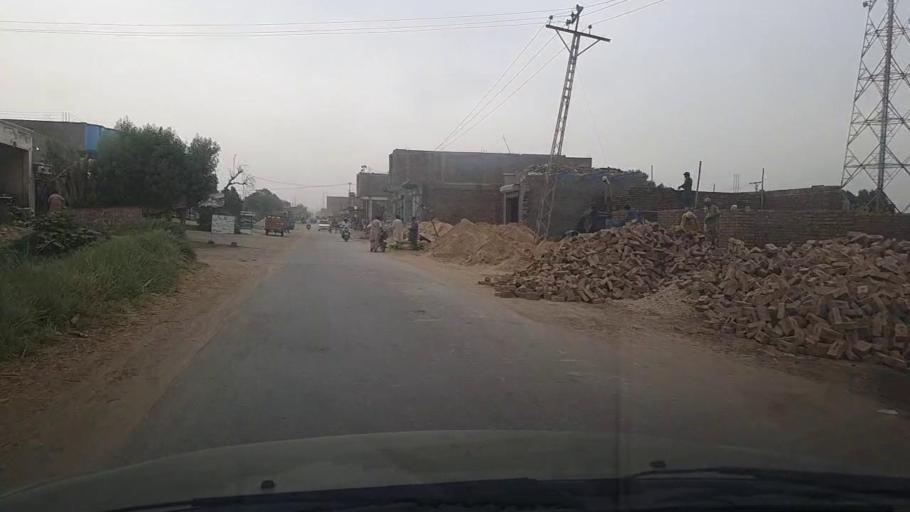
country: PK
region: Sindh
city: Daur
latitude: 26.4572
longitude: 68.3040
